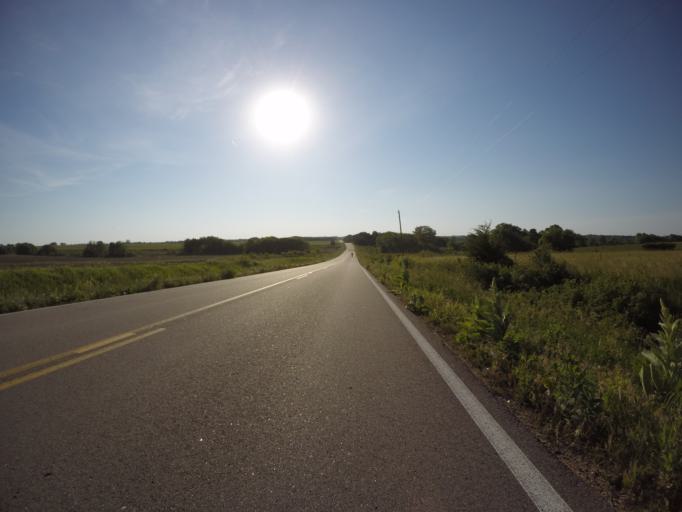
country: US
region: Nebraska
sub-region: Gage County
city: Wymore
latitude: 40.1028
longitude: -96.5237
